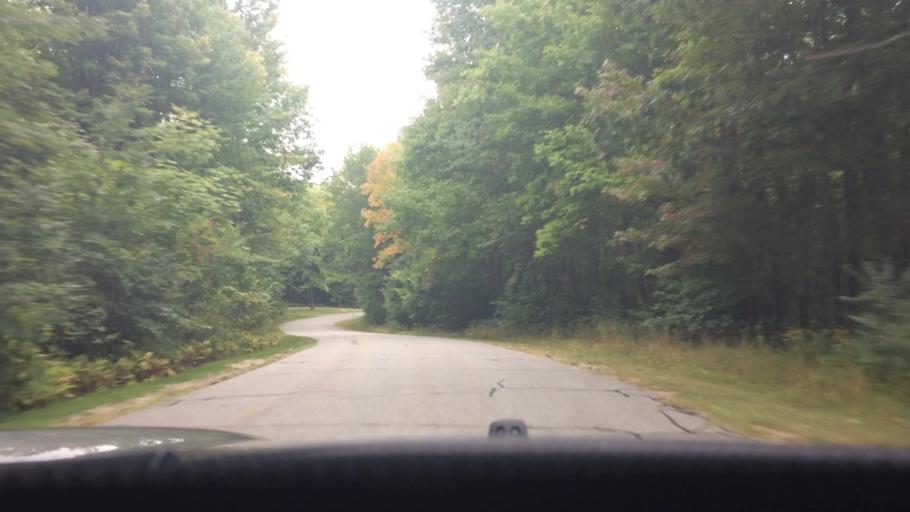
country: US
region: Maine
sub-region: Kennebec County
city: Augusta
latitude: 44.3509
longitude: -69.7891
